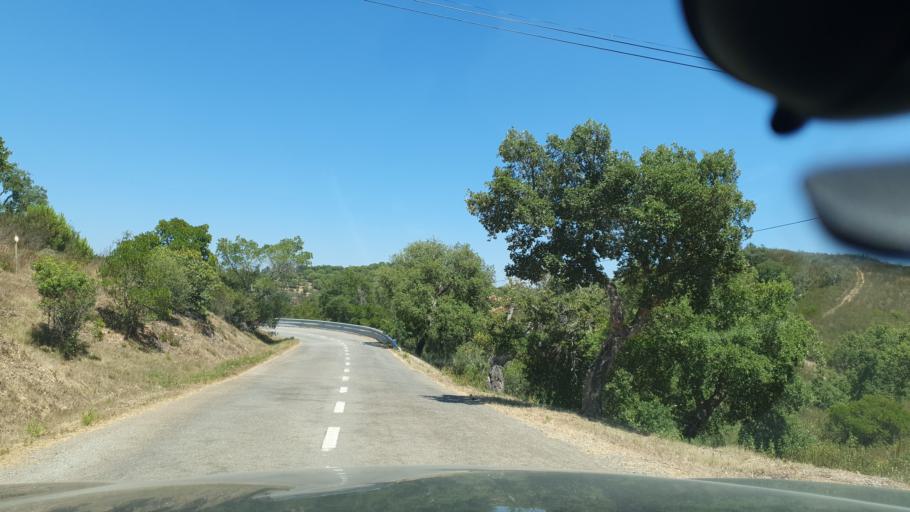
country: PT
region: Beja
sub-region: Odemira
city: Odemira
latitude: 37.6001
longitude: -8.5713
